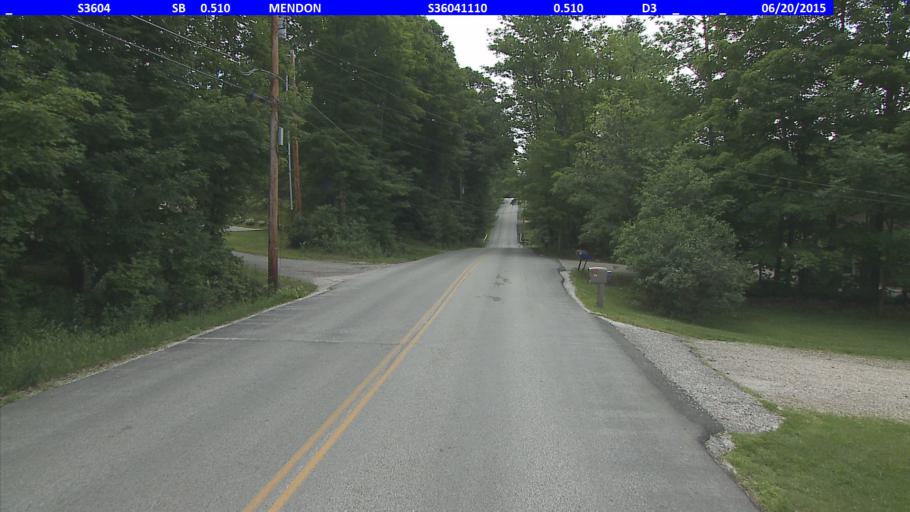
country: US
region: Vermont
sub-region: Rutland County
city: Rutland
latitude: 43.6295
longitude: -72.9371
